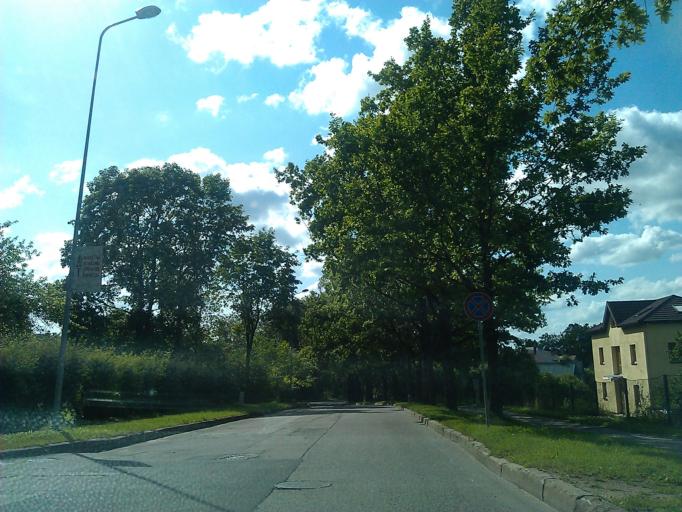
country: LV
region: Cesu Rajons
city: Cesis
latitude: 57.3076
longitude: 25.2743
